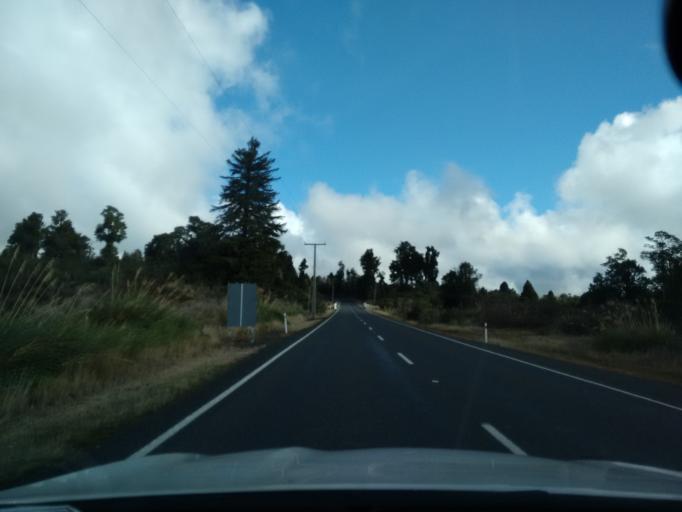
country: NZ
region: Manawatu-Wanganui
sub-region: Ruapehu District
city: Waiouru
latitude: -39.2336
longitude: 175.3932
